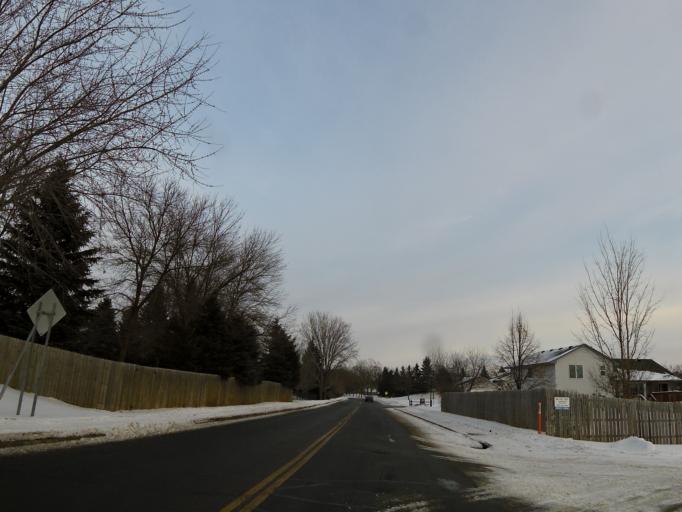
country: US
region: Minnesota
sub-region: Carver County
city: Carver
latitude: 44.7611
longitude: -93.6411
